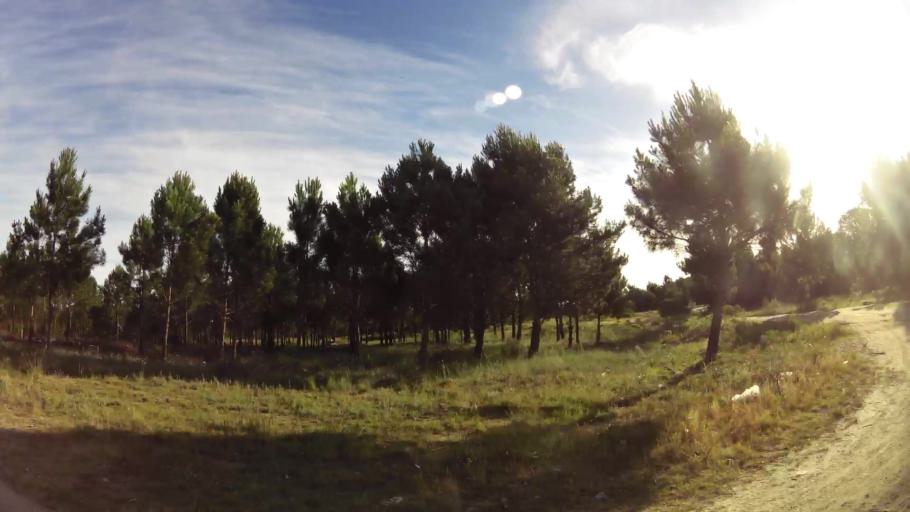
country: UY
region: Canelones
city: Empalme Olmos
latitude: -34.7633
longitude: -55.8565
